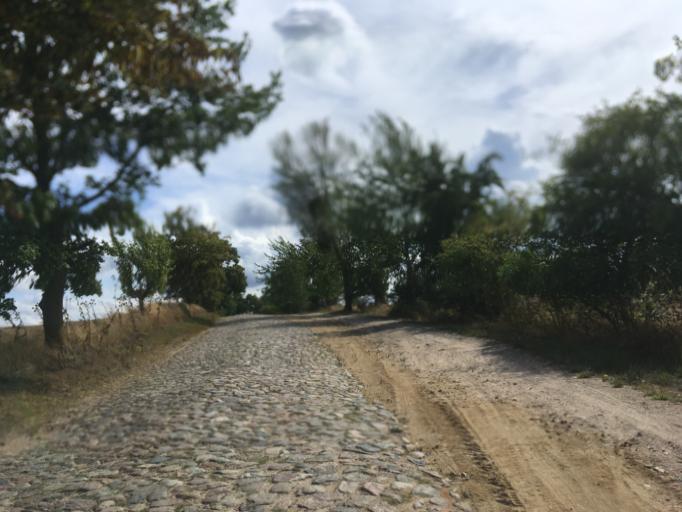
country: DE
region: Brandenburg
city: Gerswalde
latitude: 53.1289
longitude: 13.8004
